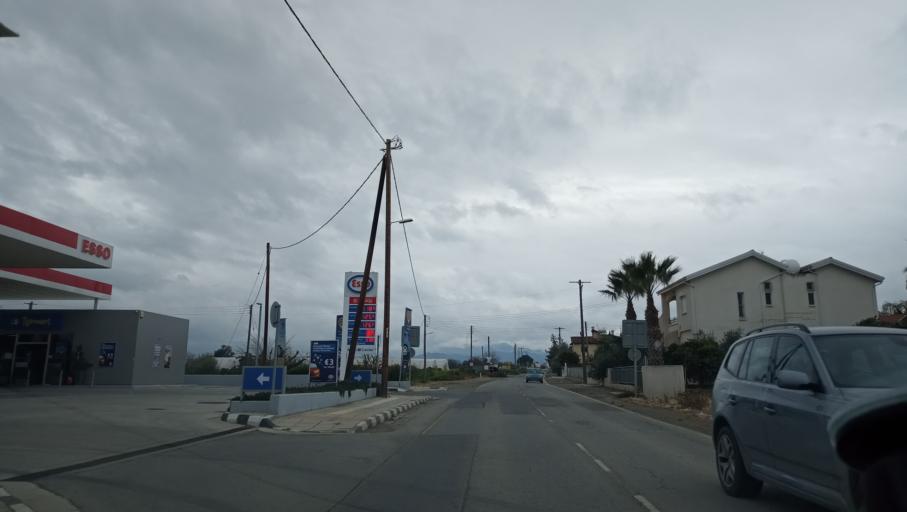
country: CY
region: Lefkosia
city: Kato Deftera
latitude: 35.0811
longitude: 33.2734
